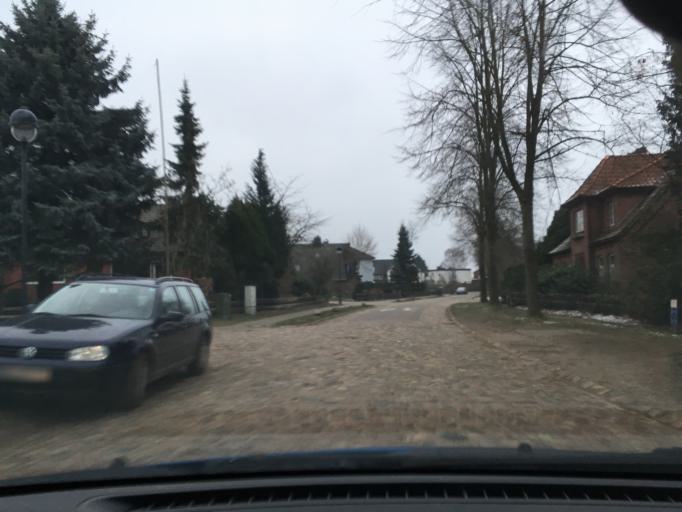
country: DE
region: Lower Saxony
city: Stelle
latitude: 53.3627
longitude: 10.1429
